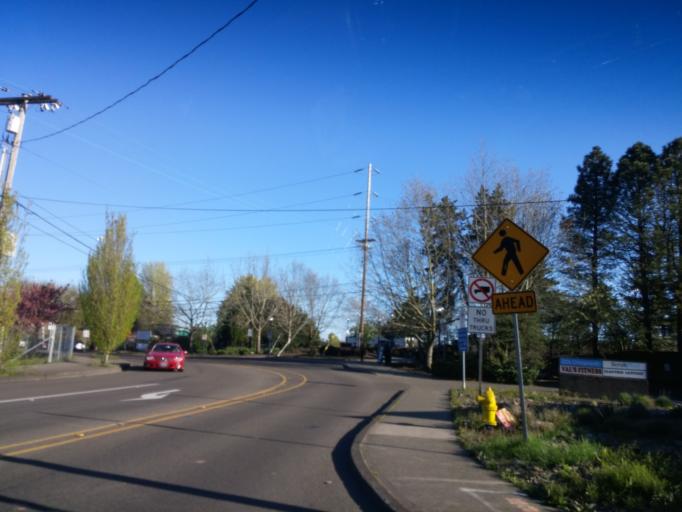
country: US
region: Oregon
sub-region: Washington County
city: Cedar Hills
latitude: 45.5093
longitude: -122.7834
